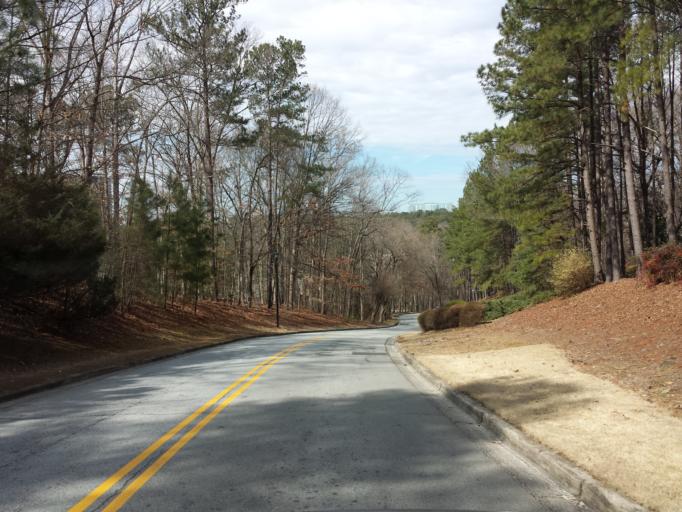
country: US
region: Georgia
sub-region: Cobb County
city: Vinings
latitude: 33.8915
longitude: -84.4525
